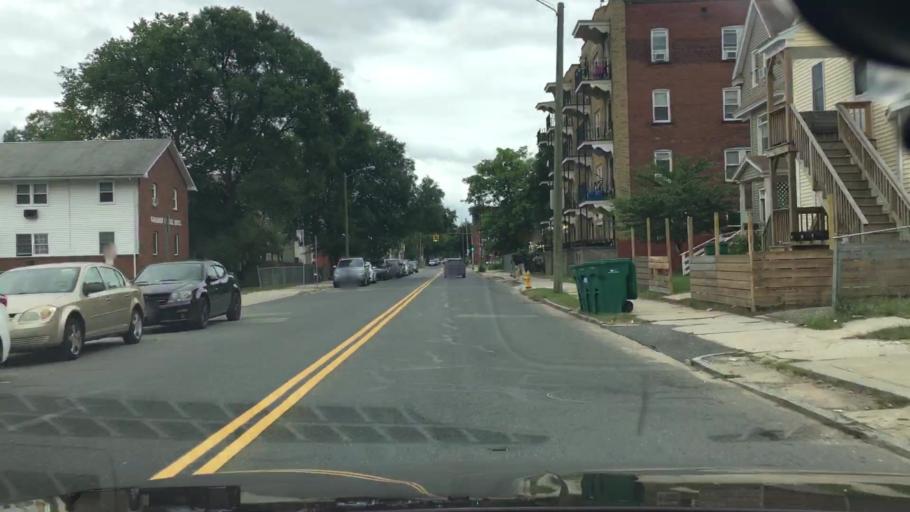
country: US
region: Massachusetts
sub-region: Hampden County
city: Springfield
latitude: 42.0941
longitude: -72.5581
